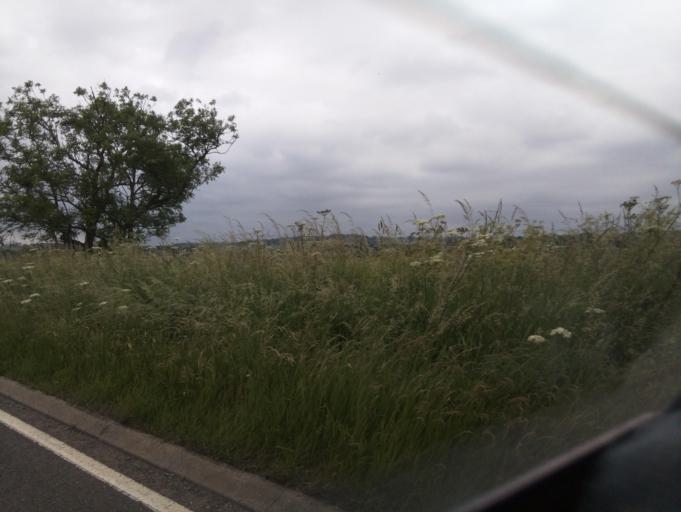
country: GB
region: England
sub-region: Leicestershire
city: Melton Mowbray
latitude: 52.7385
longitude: -0.8587
